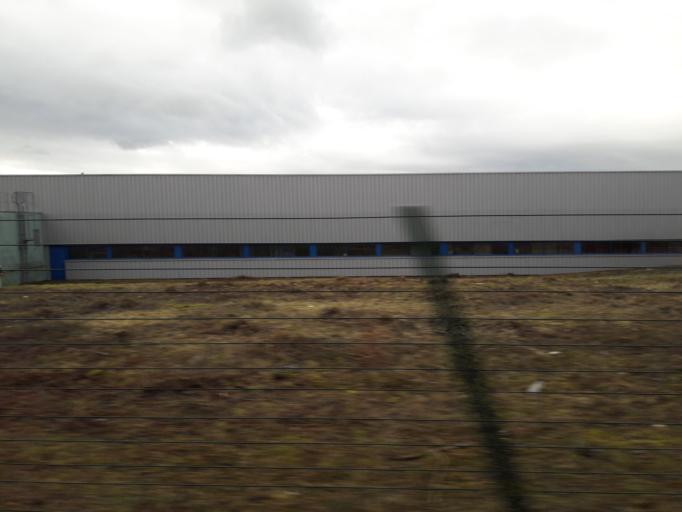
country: FR
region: Franche-Comte
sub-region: Territoire de Belfort
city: Delle
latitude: 47.5145
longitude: 7.0044
